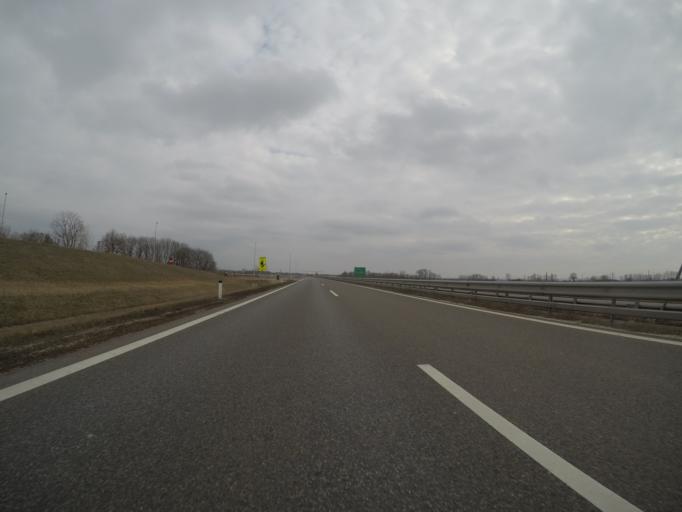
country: SI
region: Turnisce
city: Turnisce
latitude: 46.6180
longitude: 16.3037
